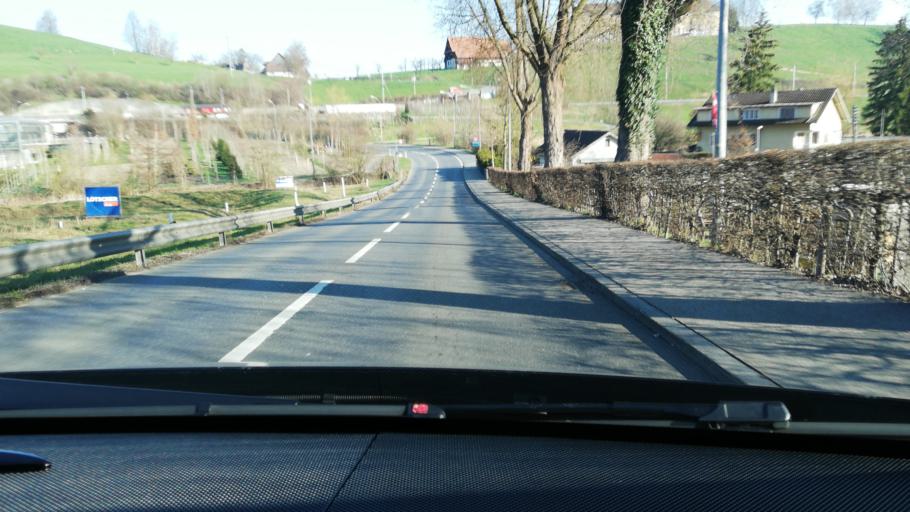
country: CH
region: Lucerne
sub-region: Lucerne-Stadt District
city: Luzern
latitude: 47.0623
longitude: 8.2984
